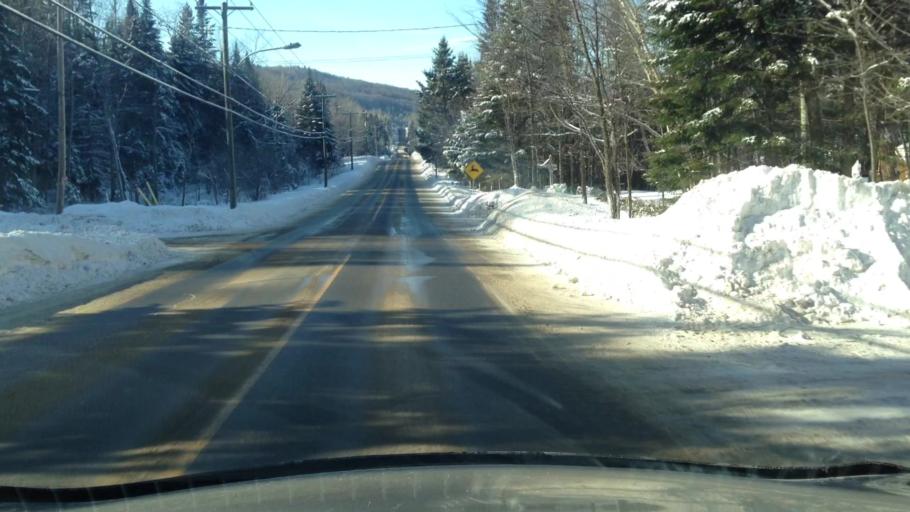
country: CA
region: Quebec
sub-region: Laurentides
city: Sainte-Agathe-des-Monts
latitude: 45.9299
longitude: -74.4138
